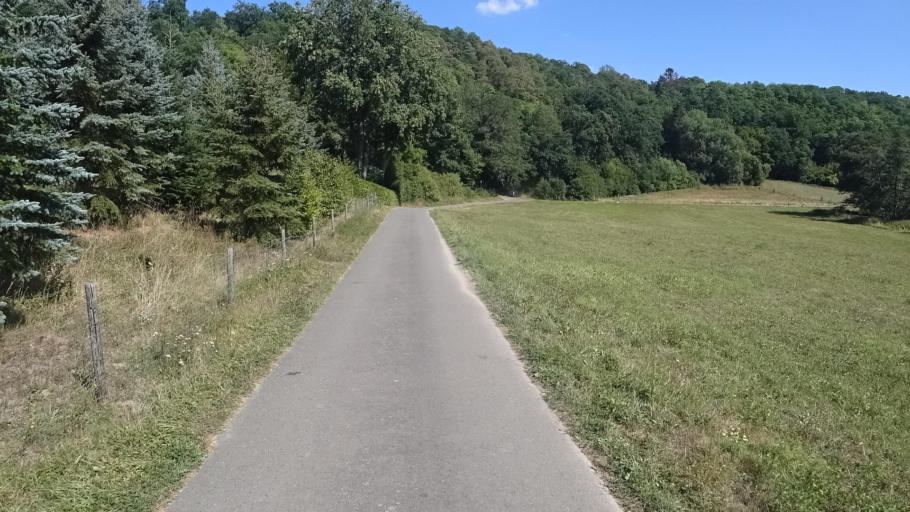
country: DE
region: Rheinland-Pfalz
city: Ravengiersburg
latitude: 49.9341
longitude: 7.4824
